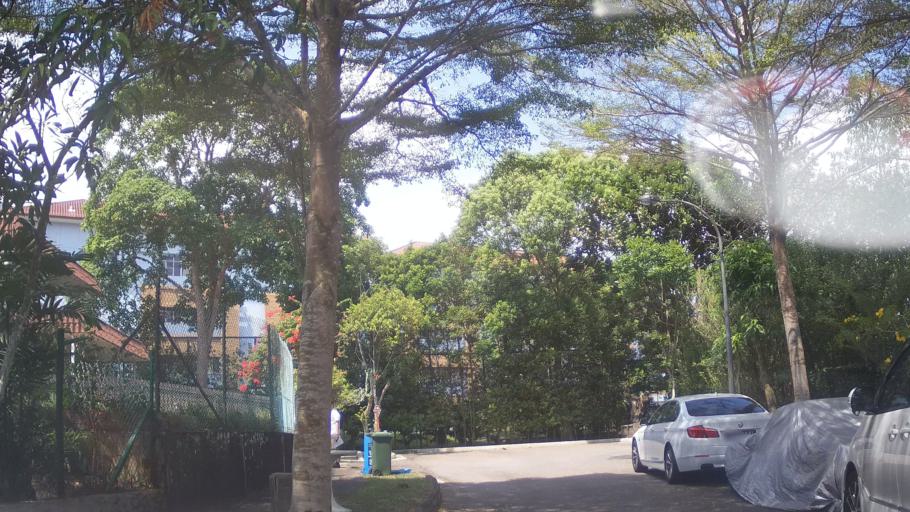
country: MY
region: Johor
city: Johor Bahru
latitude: 1.3680
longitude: 103.7711
